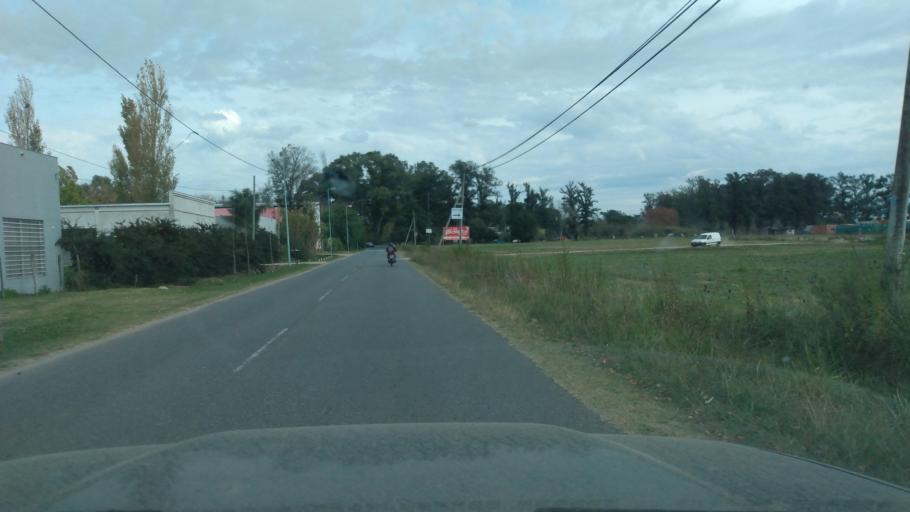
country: AR
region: Buenos Aires
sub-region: Partido de Lujan
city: Lujan
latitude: -34.5834
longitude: -59.1263
